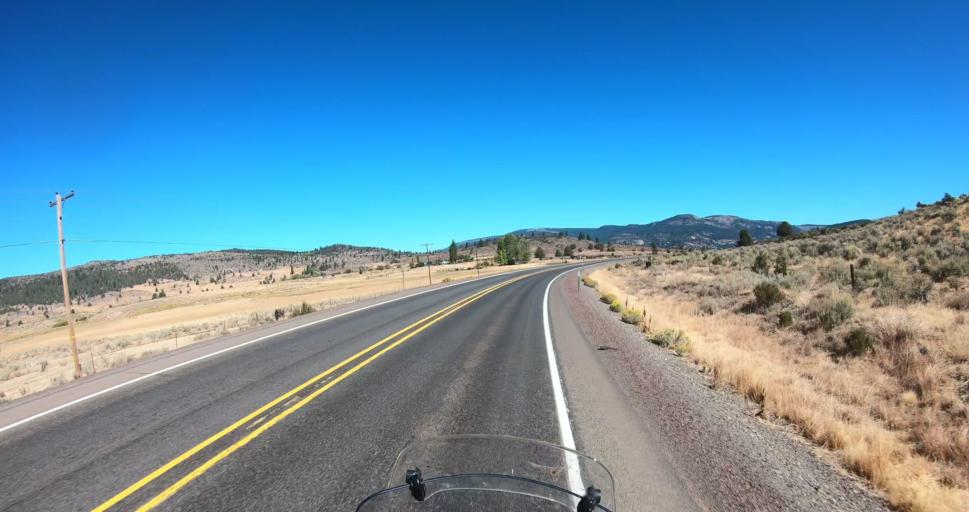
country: US
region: Oregon
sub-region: Lake County
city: Lakeview
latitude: 42.3227
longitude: -120.3299
